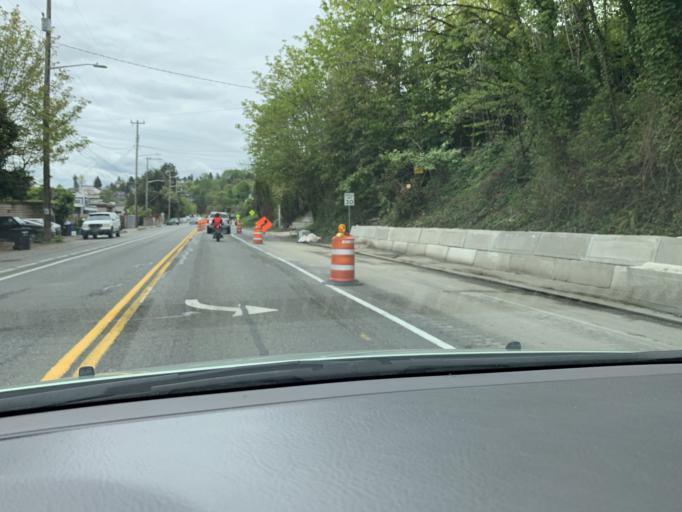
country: US
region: Washington
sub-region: King County
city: Bryn Mawr-Skyway
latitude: 47.5143
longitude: -122.2519
